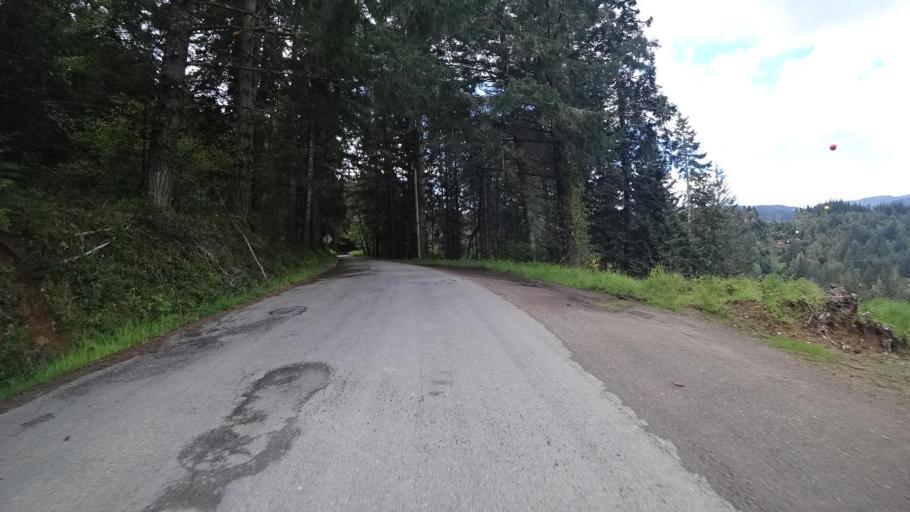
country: US
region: California
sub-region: Humboldt County
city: Blue Lake
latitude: 40.7679
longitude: -123.8762
